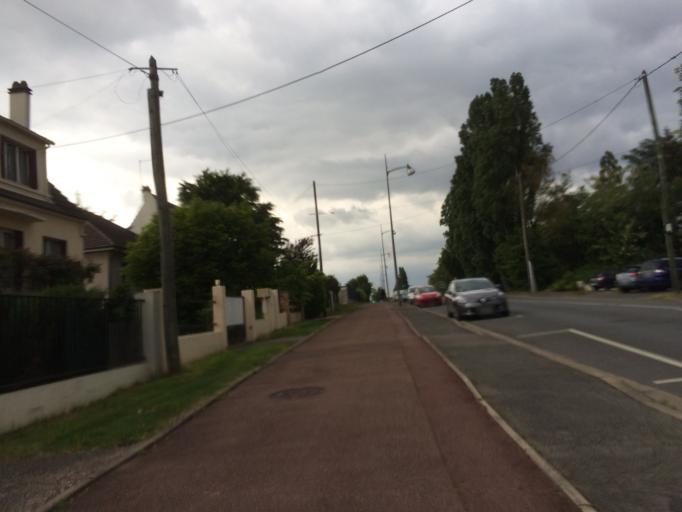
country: FR
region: Ile-de-France
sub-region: Departement de l'Essonne
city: Epinay-sur-Orge
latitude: 48.6837
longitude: 2.3092
